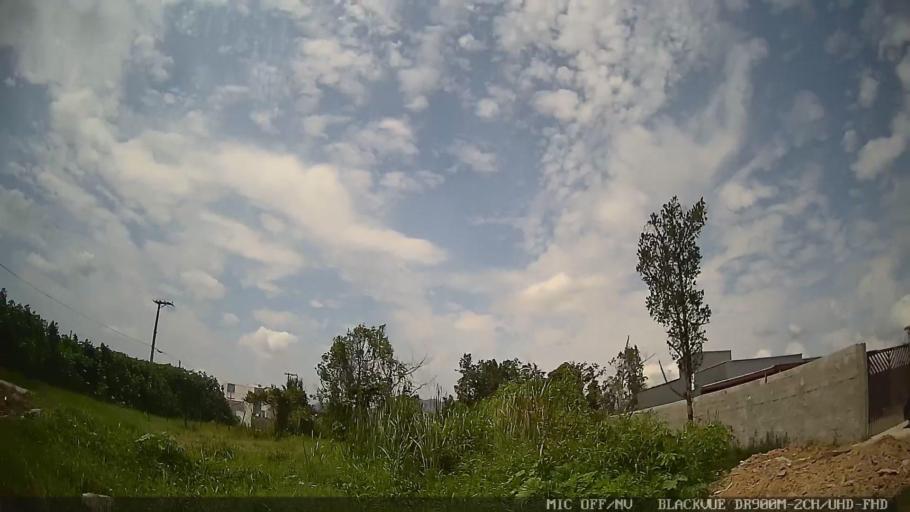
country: BR
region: Sao Paulo
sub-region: Caraguatatuba
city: Caraguatatuba
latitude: -23.6712
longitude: -45.4573
